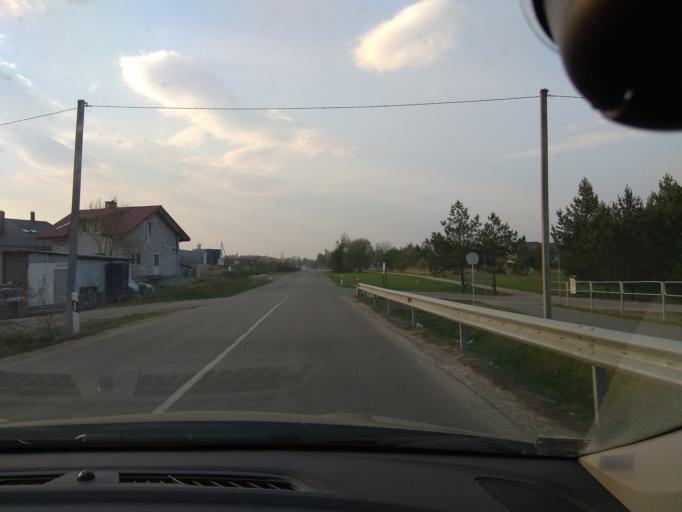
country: LT
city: Grigiskes
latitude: 54.6207
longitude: 25.1139
